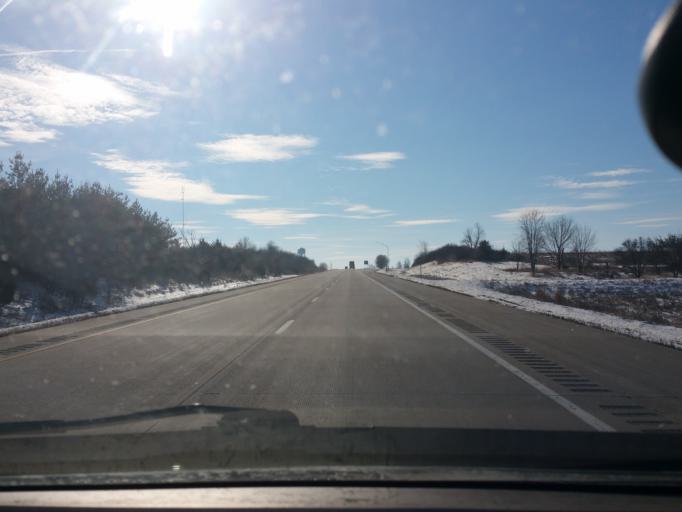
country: US
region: Iowa
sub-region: Clarke County
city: Osceola
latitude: 40.9976
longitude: -93.8000
